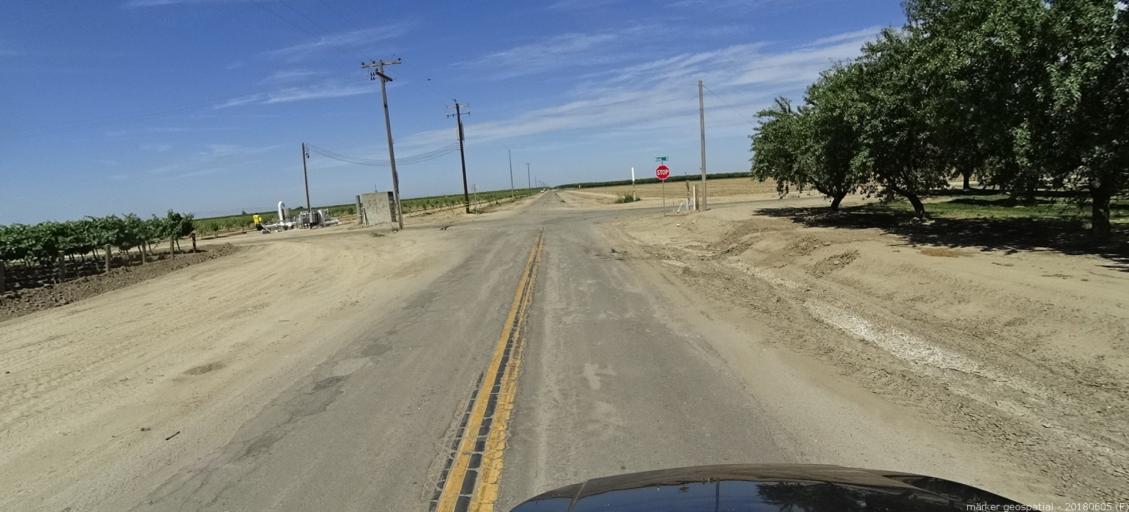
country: US
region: California
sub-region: Madera County
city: Chowchilla
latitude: 37.0982
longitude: -120.3647
